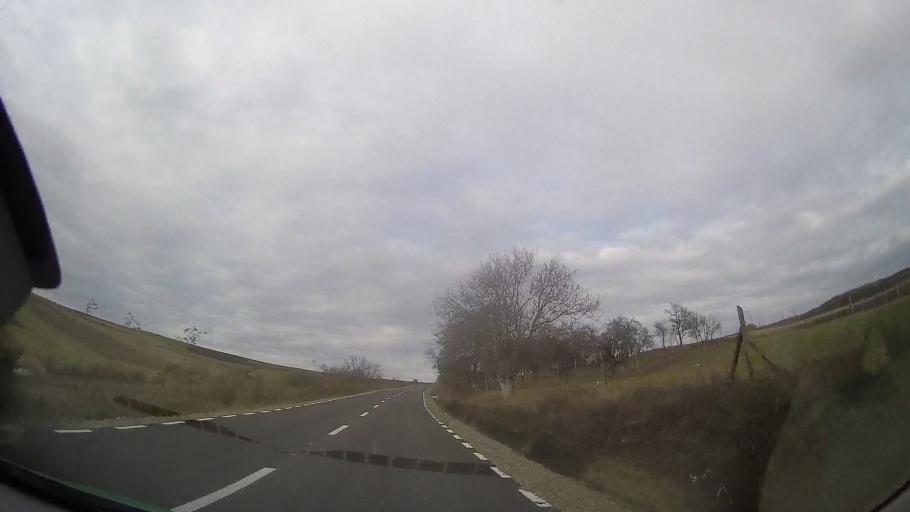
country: RO
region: Bistrita-Nasaud
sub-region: Comuna Teaca
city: Ocnita
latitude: 46.8232
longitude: 24.4817
